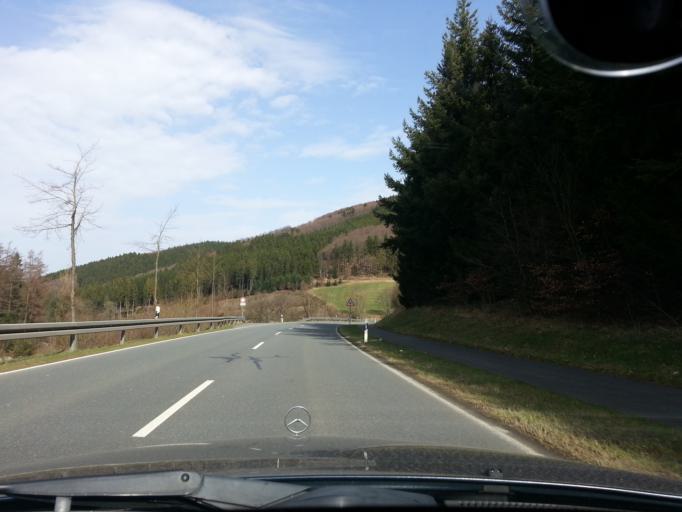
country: DE
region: North Rhine-Westphalia
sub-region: Regierungsbezirk Arnsberg
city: Bad Fredeburg
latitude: 51.2719
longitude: 8.3530
